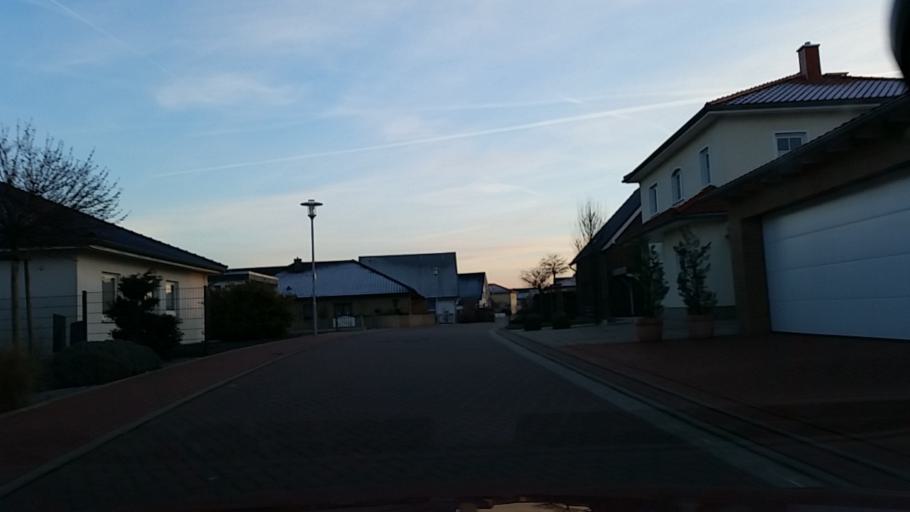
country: DE
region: Lower Saxony
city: Weyhausen
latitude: 52.4018
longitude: 10.7055
